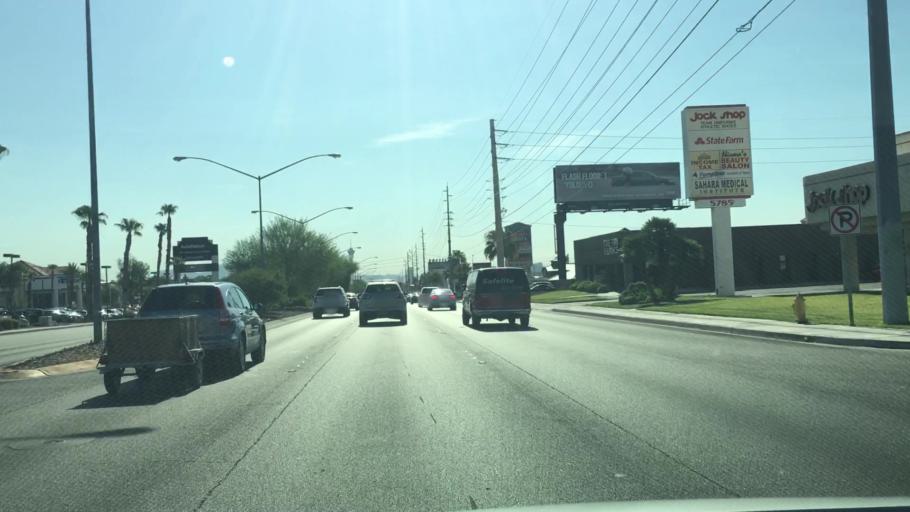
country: US
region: Nevada
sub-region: Clark County
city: Spring Valley
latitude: 36.1442
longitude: -115.2210
